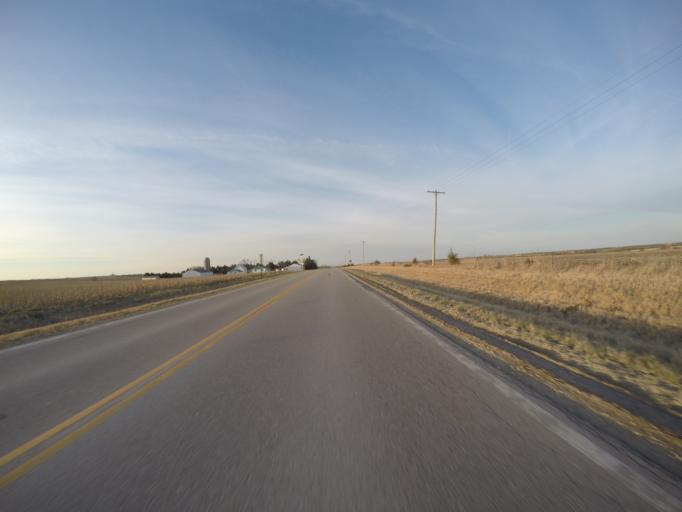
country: US
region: Kansas
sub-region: Riley County
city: Fort Riley North
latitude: 39.3371
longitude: -96.8306
